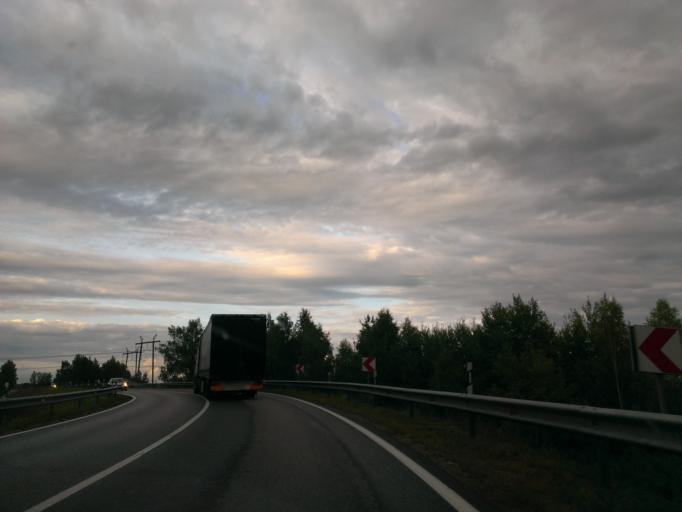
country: LV
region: Salaspils
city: Salaspils
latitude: 56.8449
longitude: 24.3958
